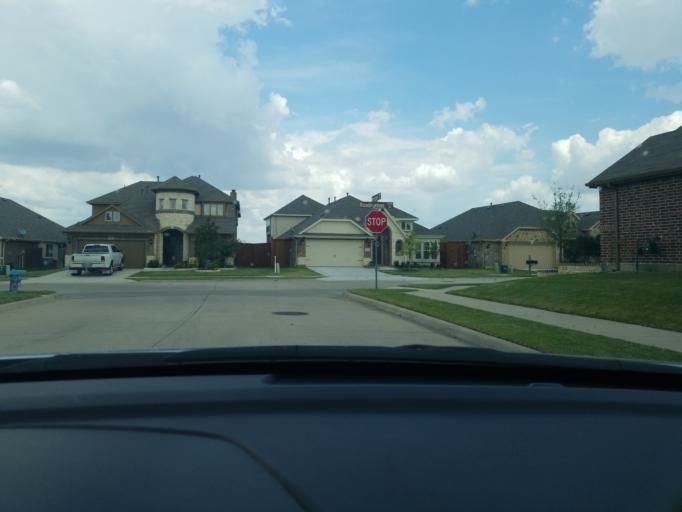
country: US
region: Texas
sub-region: Denton County
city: Little Elm
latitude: 33.2086
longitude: -96.9327
